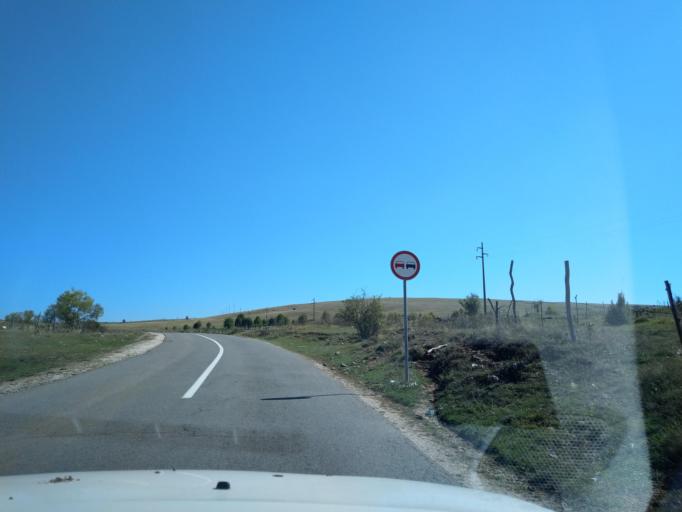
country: RS
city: Sokolovica
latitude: 43.2745
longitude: 20.2008
